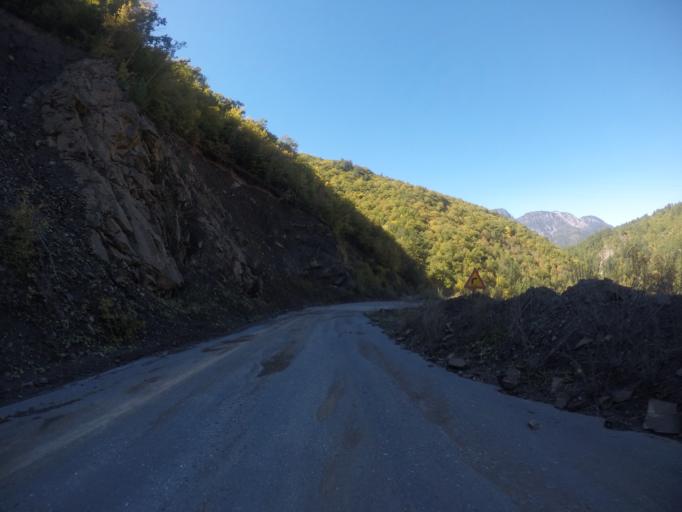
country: GR
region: Epirus
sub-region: Nomos Ioanninon
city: Konitsa
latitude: 40.0217
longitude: 20.8898
